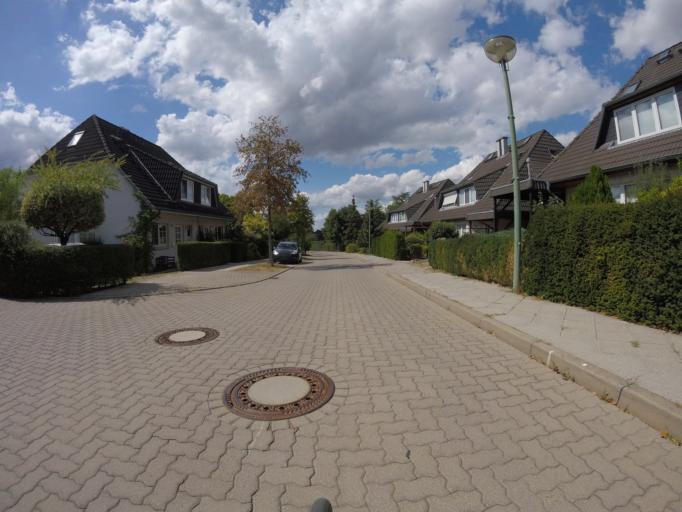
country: DE
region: Brandenburg
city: Werder
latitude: 52.4129
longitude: 12.9920
